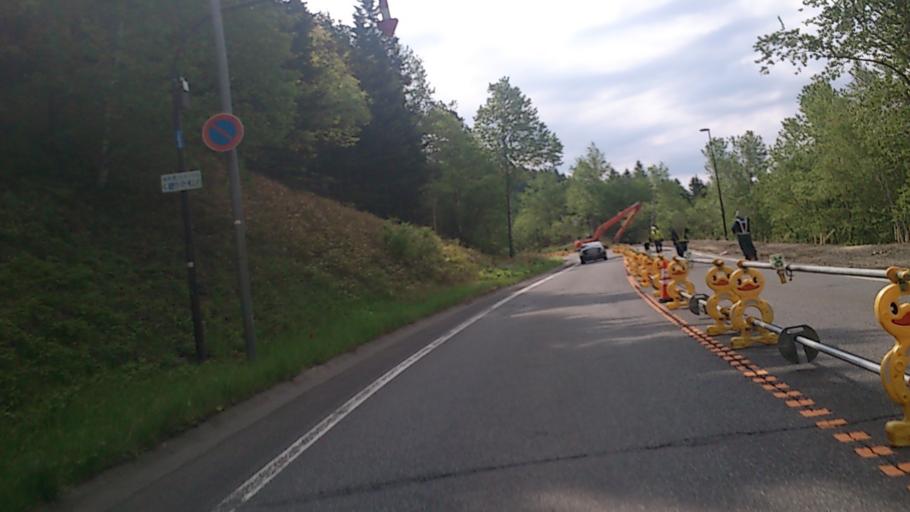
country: JP
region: Hokkaido
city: Kamikawa
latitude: 43.6846
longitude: 143.0323
